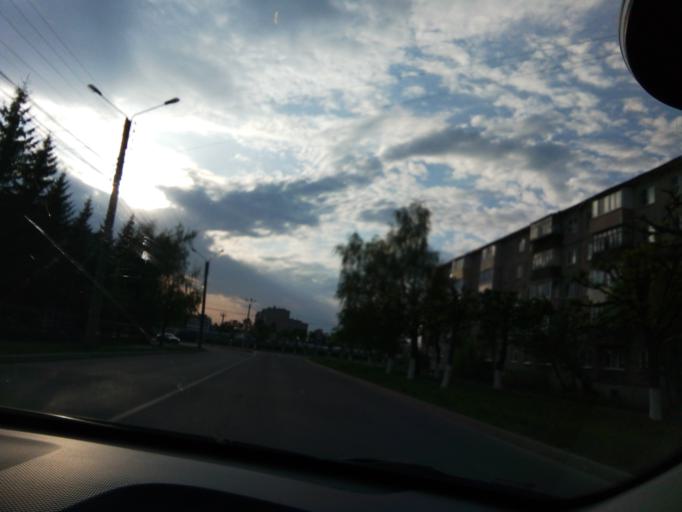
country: RU
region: Chuvashia
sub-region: Cheboksarskiy Rayon
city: Cheboksary
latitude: 56.1225
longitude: 47.2765
